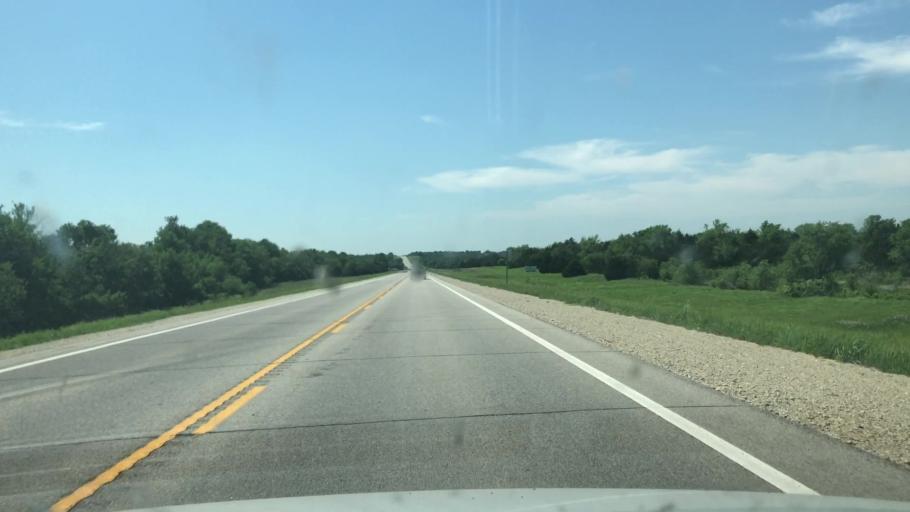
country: US
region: Kansas
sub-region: Cowley County
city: Winfield
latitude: 37.3672
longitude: -97.0072
